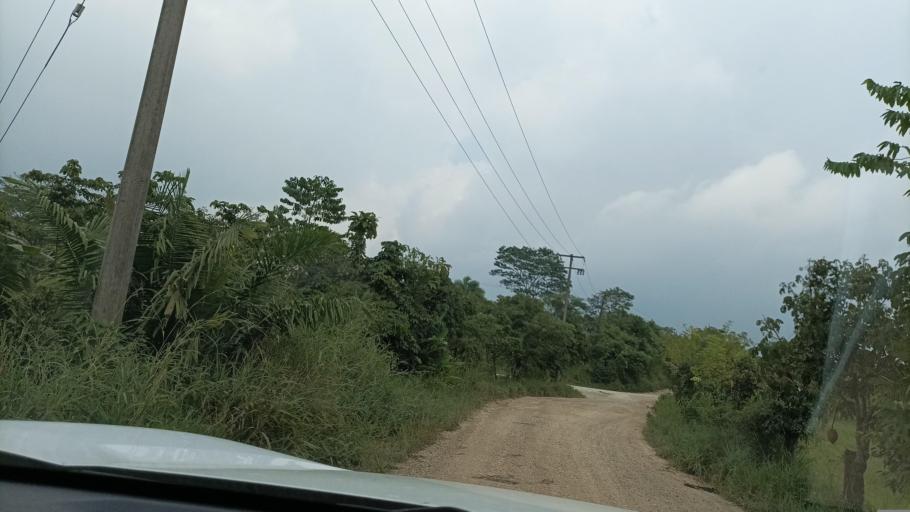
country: MX
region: Tabasco
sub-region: Huimanguillo
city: Francisco Rueda
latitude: 17.5994
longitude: -94.1957
